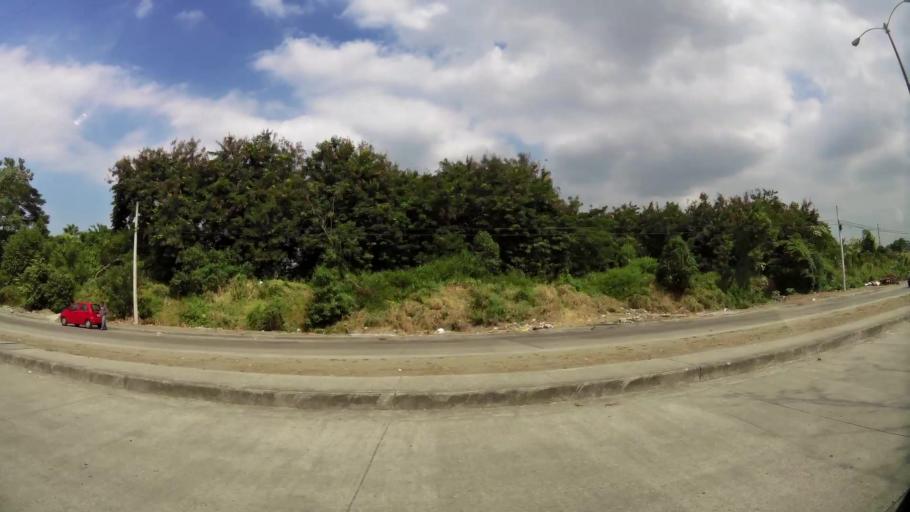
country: EC
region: Guayas
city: Santa Lucia
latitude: -2.0931
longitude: -79.9456
